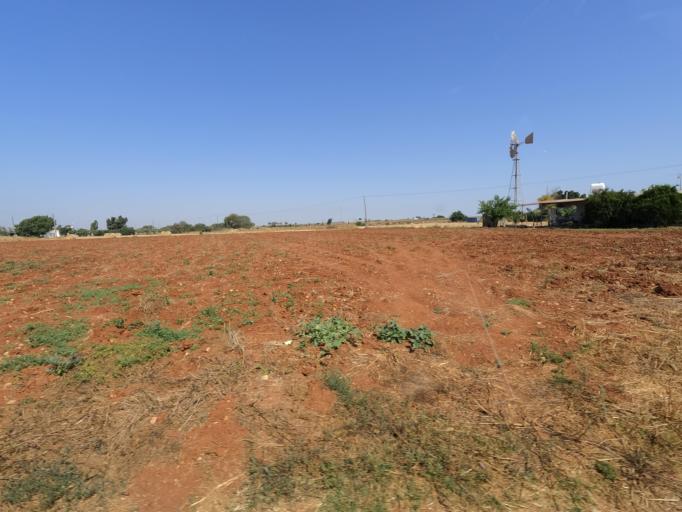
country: CY
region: Ammochostos
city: Frenaros
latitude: 34.9983
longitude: 33.9389
